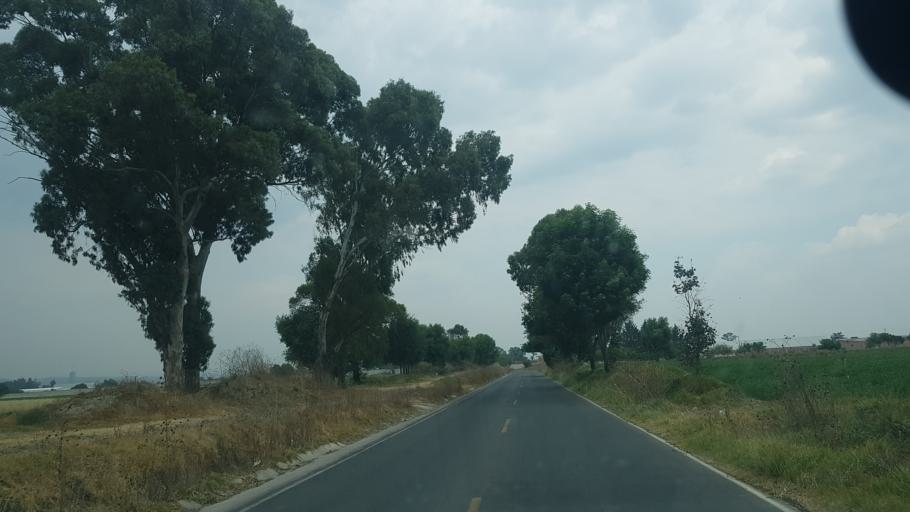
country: MX
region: Puebla
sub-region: Huejotzingo
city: San Mateo Capultitlan
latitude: 19.2033
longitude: -98.4285
